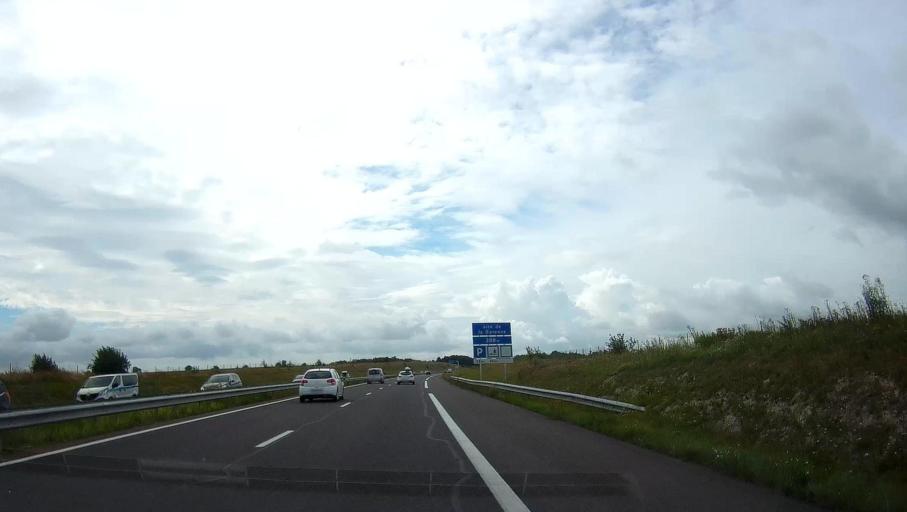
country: FR
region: Champagne-Ardenne
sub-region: Departement de la Marne
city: Fagnieres
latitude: 48.9570
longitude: 4.2883
